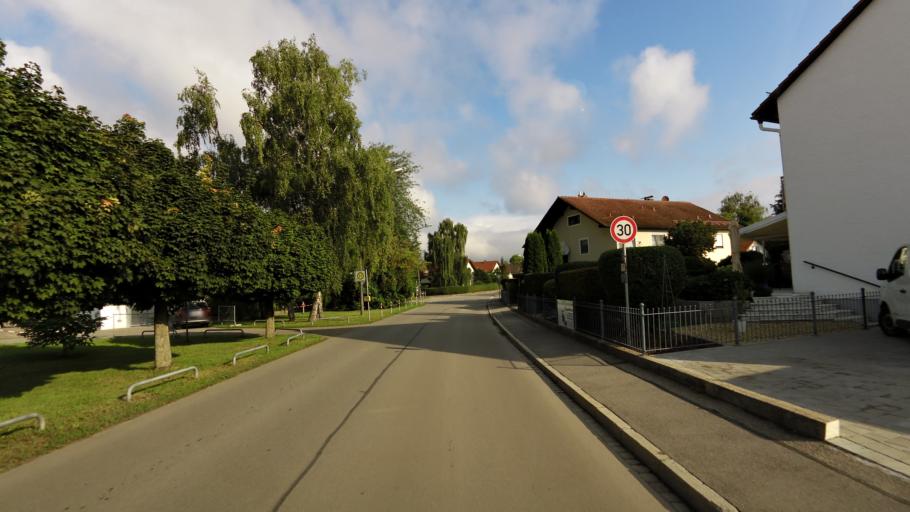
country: DE
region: Bavaria
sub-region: Lower Bavaria
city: Straubing
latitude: 48.8911
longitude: 12.5635
